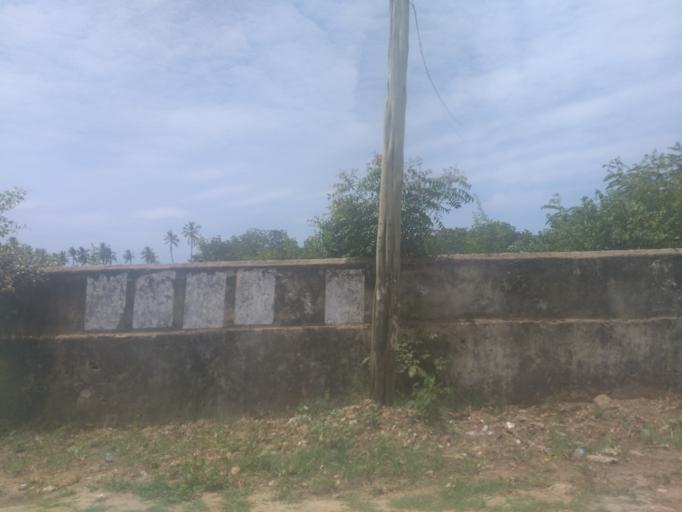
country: TZ
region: Zanzibar Urban/West
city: Zanzibar
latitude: -6.2144
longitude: 39.2115
